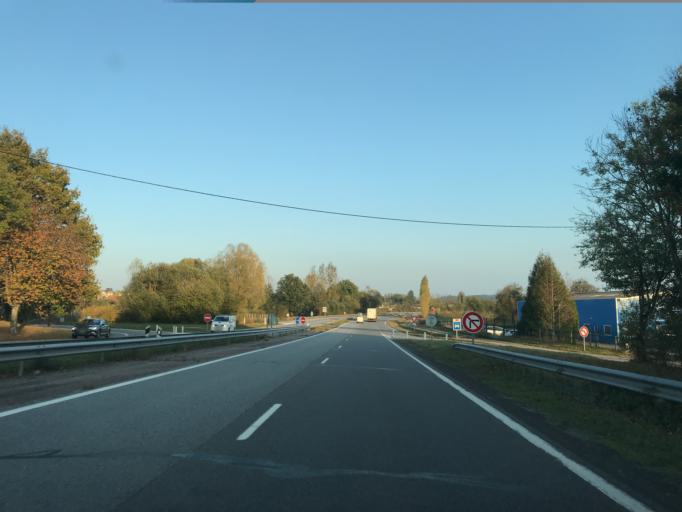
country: FR
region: Pays de la Loire
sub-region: Departement de la Sarthe
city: Mamers
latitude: 48.5099
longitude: 0.3448
